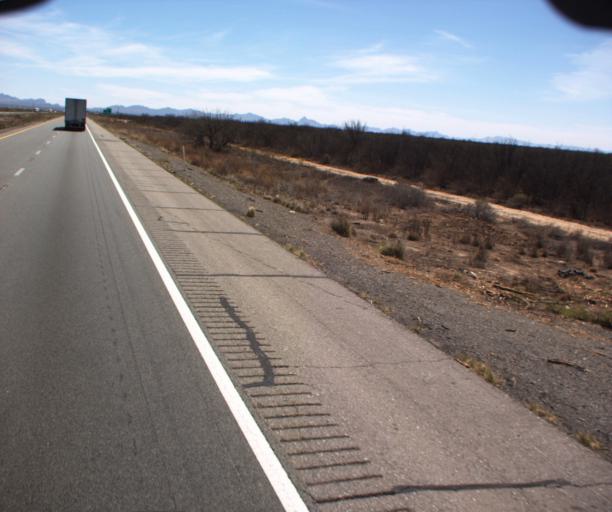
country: US
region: Arizona
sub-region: Cochise County
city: Willcox
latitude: 32.2801
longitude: -109.2795
